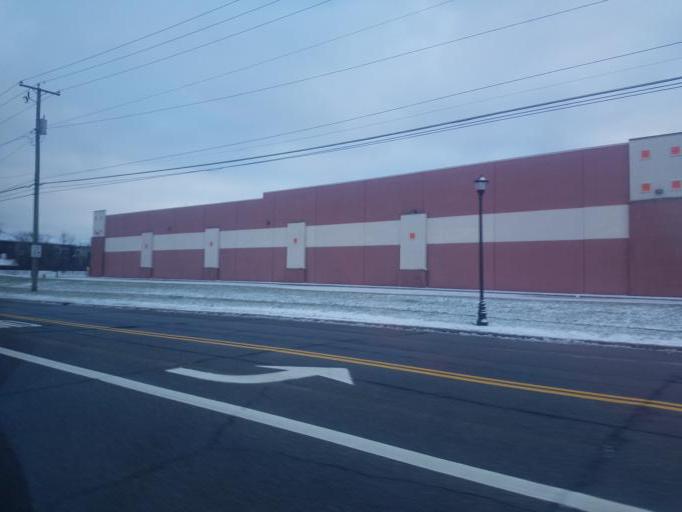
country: US
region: Ohio
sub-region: Franklin County
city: Gahanna
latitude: 40.0645
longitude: -82.8615
